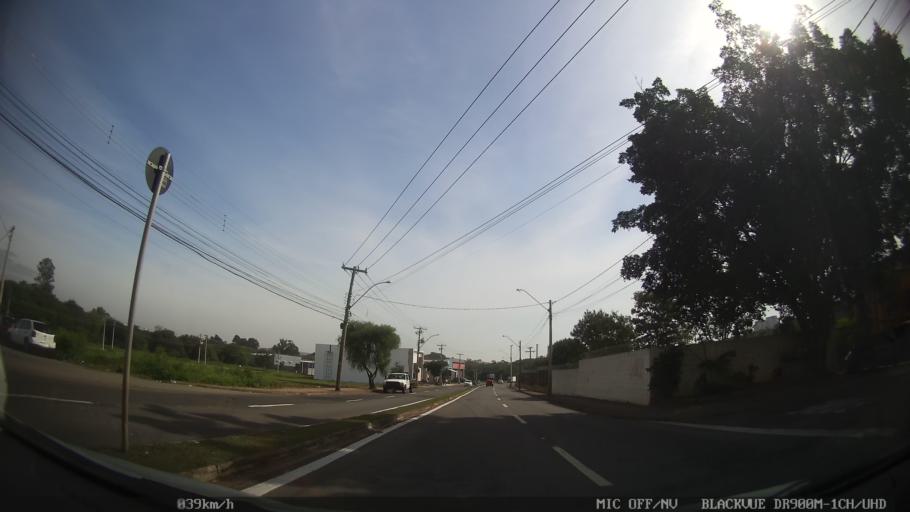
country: BR
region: Sao Paulo
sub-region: Piracicaba
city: Piracicaba
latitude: -22.6927
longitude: -47.6726
